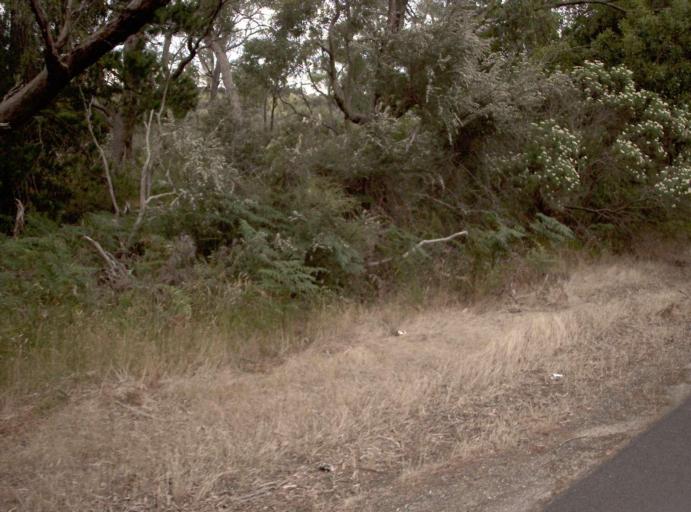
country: AU
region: Victoria
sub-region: Wellington
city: Sale
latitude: -38.2128
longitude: 147.0639
